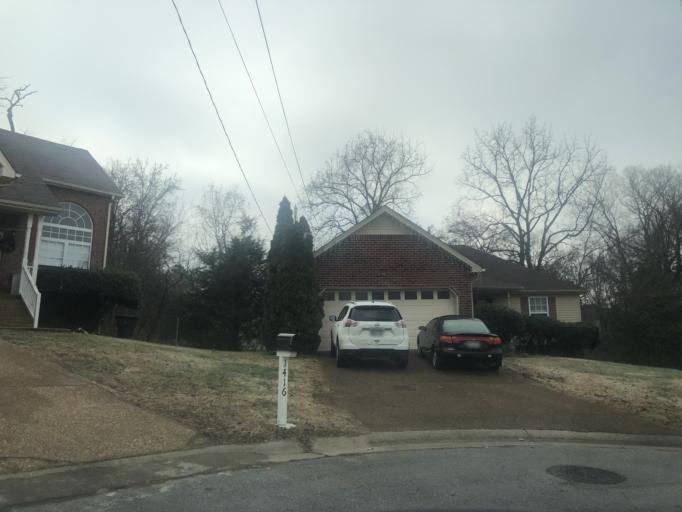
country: US
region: Tennessee
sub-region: Rutherford County
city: La Vergne
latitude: 36.0674
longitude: -86.6598
